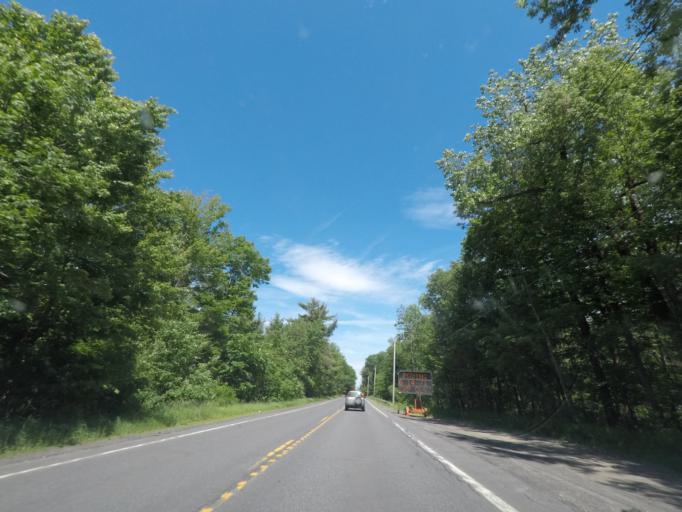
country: US
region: Massachusetts
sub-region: Berkshire County
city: West Stockbridge
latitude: 42.3346
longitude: -73.4292
